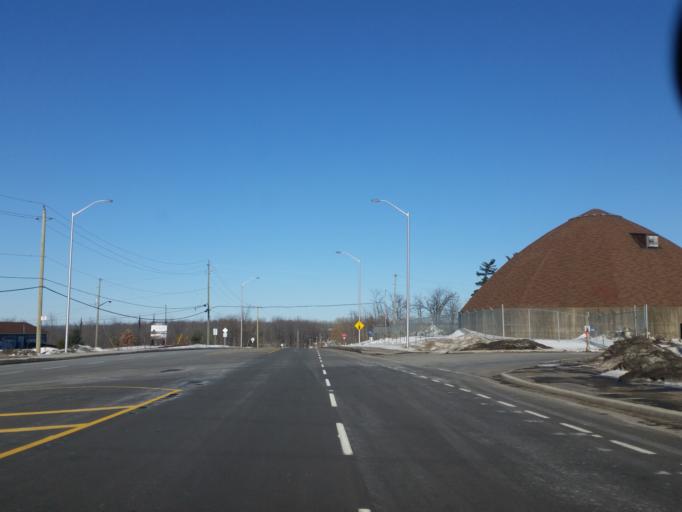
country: CA
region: Ontario
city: Clarence-Rockland
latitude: 45.4959
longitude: -75.4824
